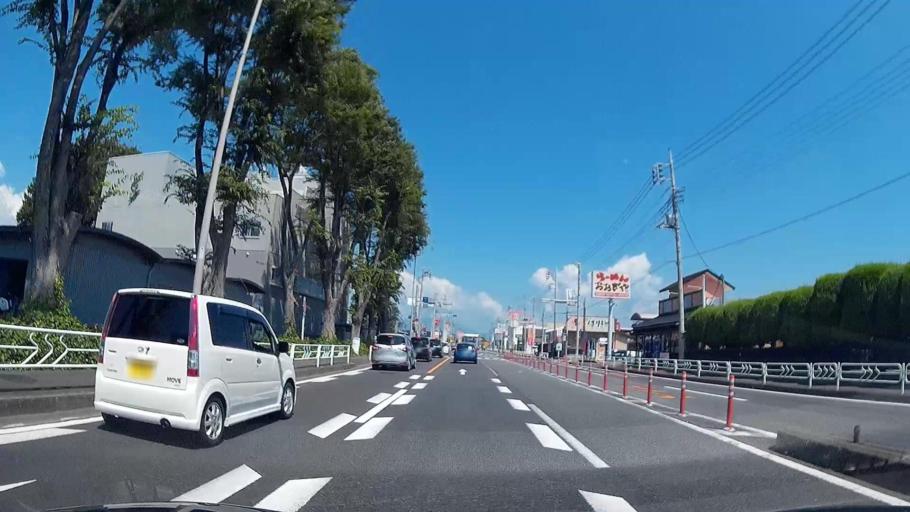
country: JP
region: Gunma
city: Maebashi-shi
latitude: 36.4324
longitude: 139.0524
